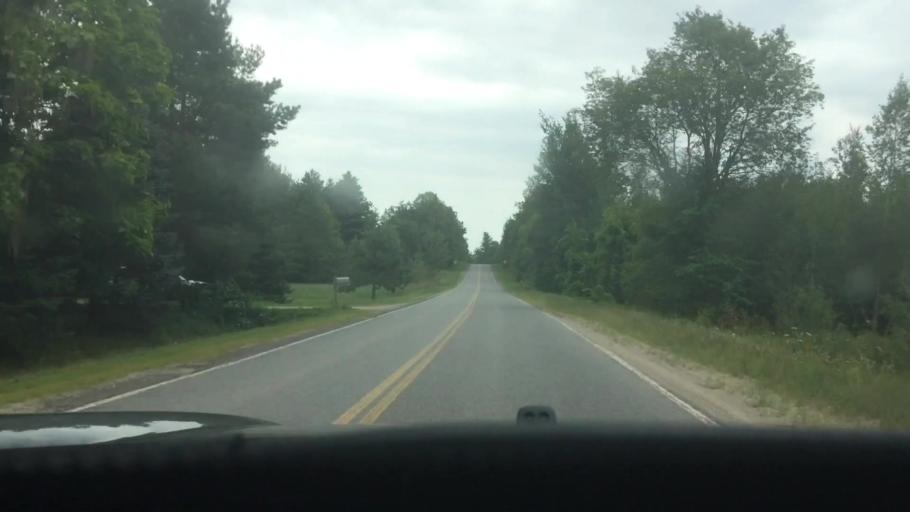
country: US
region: New York
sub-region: St. Lawrence County
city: Hannawa Falls
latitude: 44.6184
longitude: -74.8590
